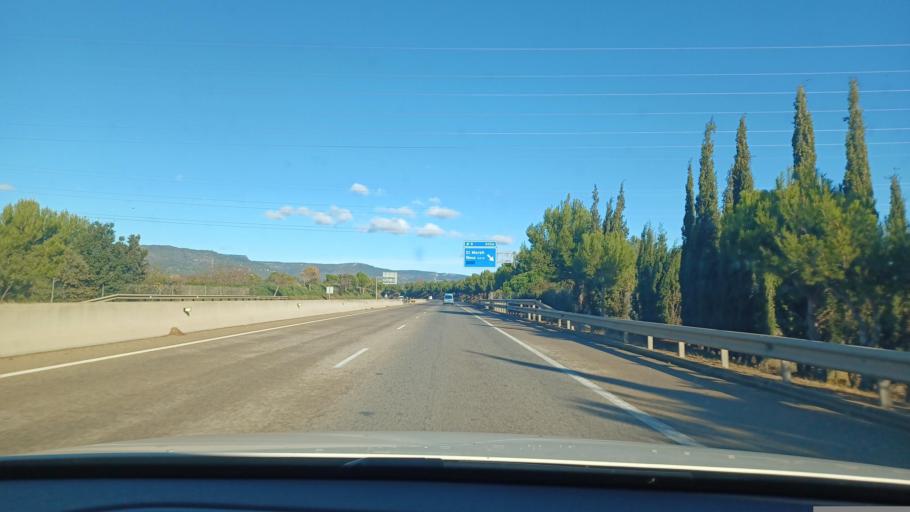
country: ES
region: Catalonia
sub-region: Provincia de Tarragona
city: Reus
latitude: 41.1606
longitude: 1.1427
